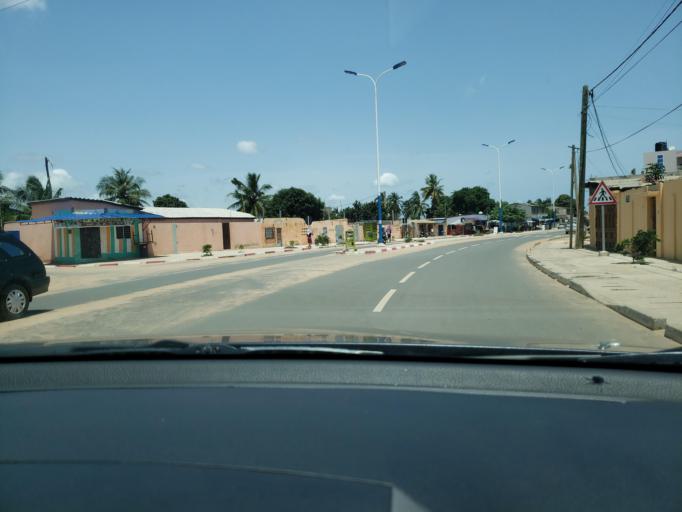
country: TG
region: Maritime
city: Lome
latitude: 6.1929
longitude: 1.1987
